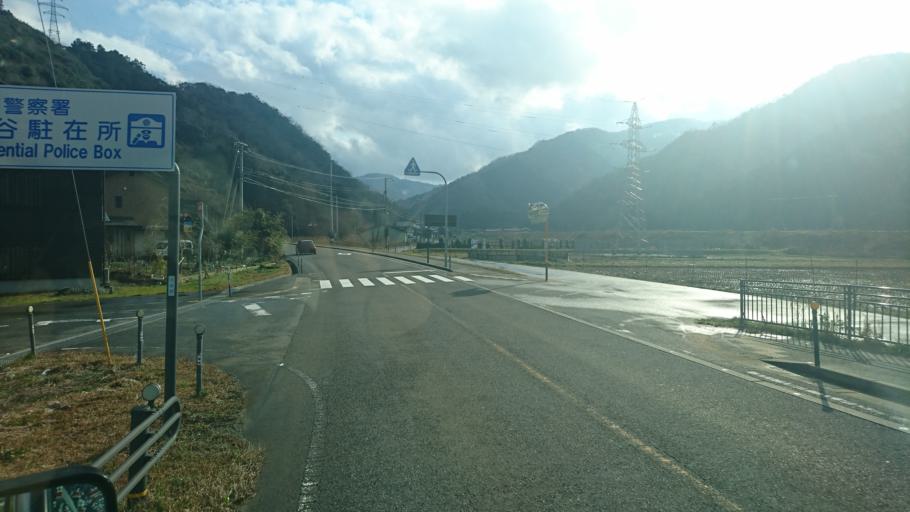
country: JP
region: Tottori
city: Tottori
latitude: 35.6070
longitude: 134.4702
